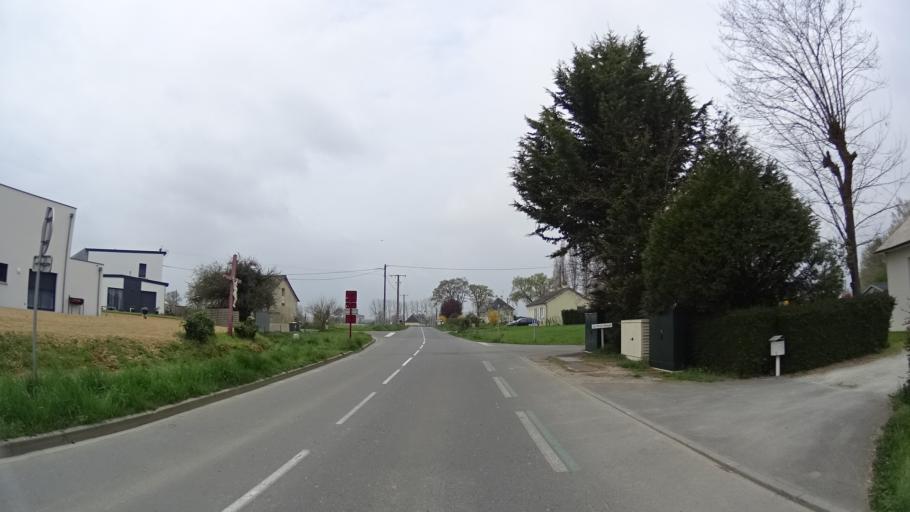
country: FR
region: Brittany
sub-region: Departement d'Ille-et-Vilaine
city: Saint-Gilles
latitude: 48.1535
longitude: -1.8410
